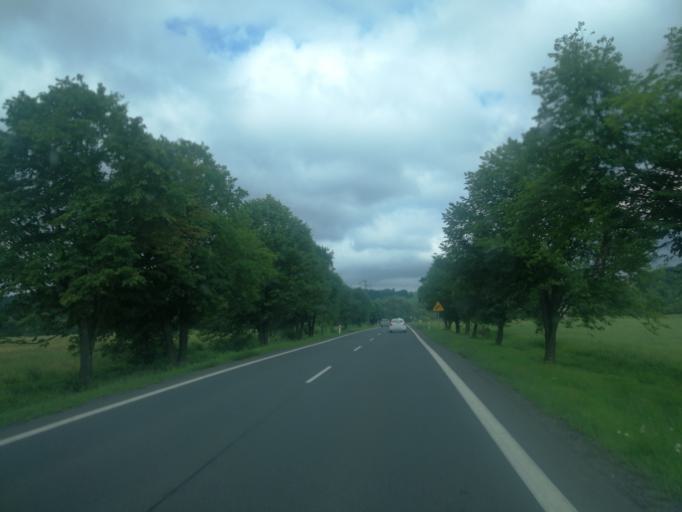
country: PL
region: Subcarpathian Voivodeship
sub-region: Powiat leski
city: Lesko
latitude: 49.4930
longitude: 22.3154
